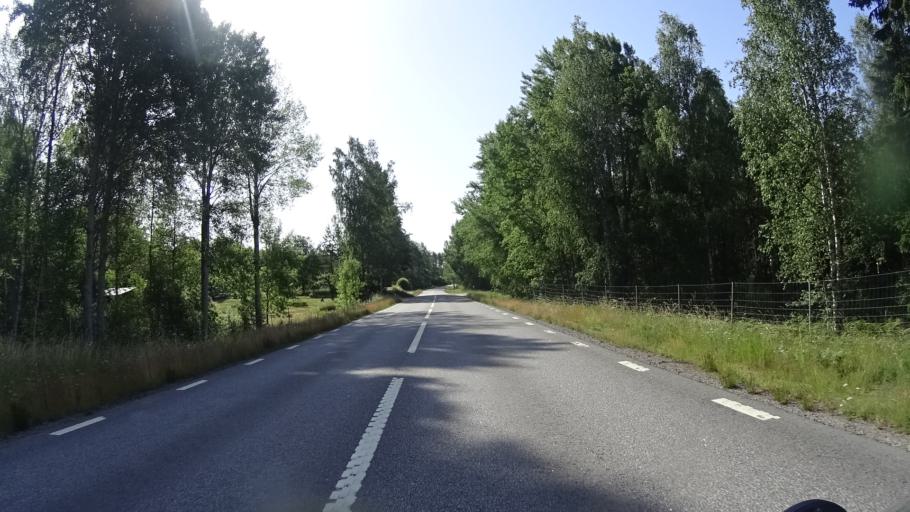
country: SE
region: OEstergoetland
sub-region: Atvidabergs Kommun
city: Atvidaberg
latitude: 58.1652
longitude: 16.0584
